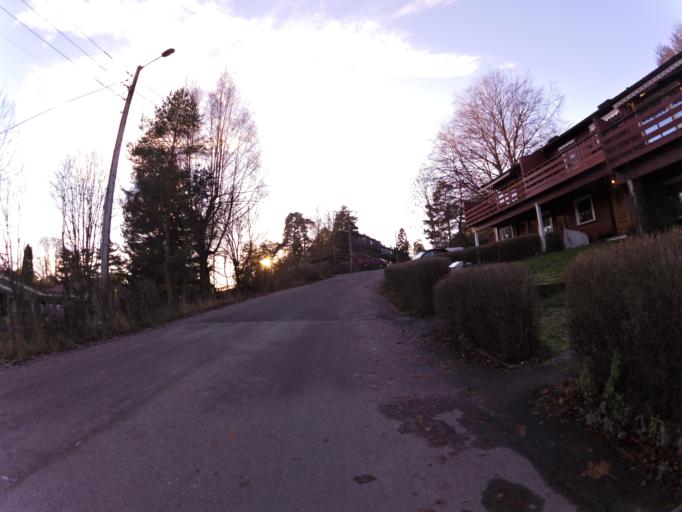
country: NO
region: Ostfold
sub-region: Fredrikstad
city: Fredrikstad
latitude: 59.2352
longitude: 10.9634
